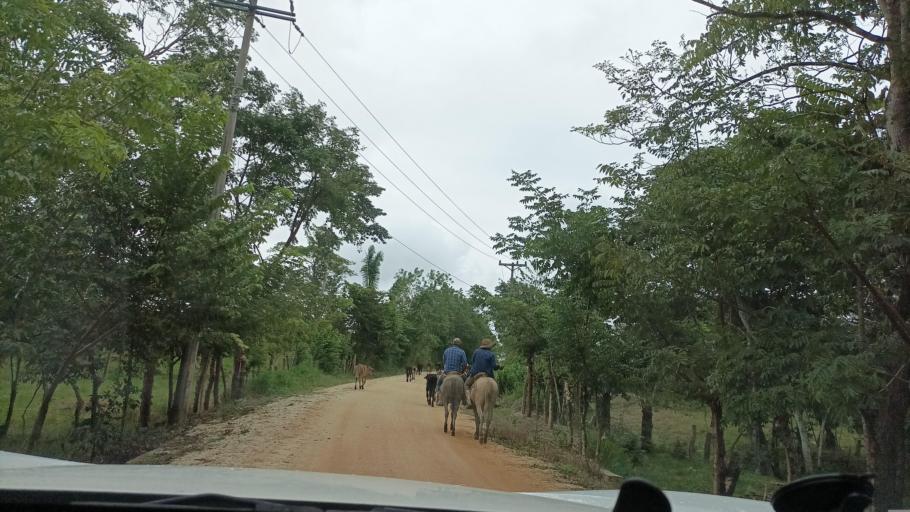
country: MX
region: Veracruz
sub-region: Moloacan
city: Cuichapa
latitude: 17.8178
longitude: -94.3548
